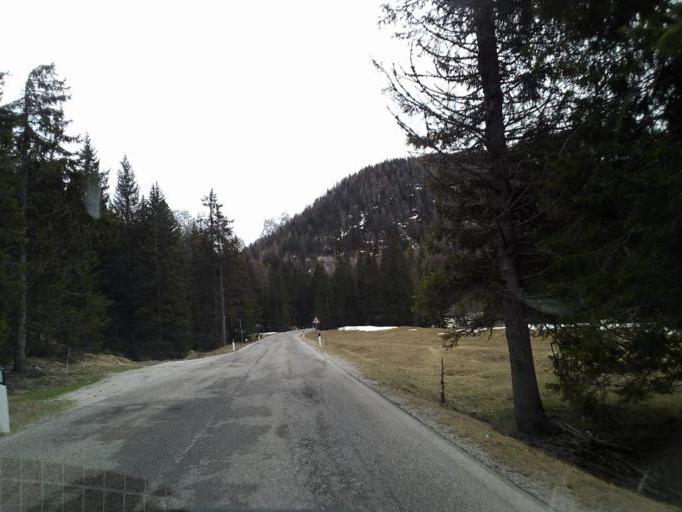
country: IT
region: Veneto
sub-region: Provincia di Belluno
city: Cortina d'Ampezzo
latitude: 46.6042
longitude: 12.2390
